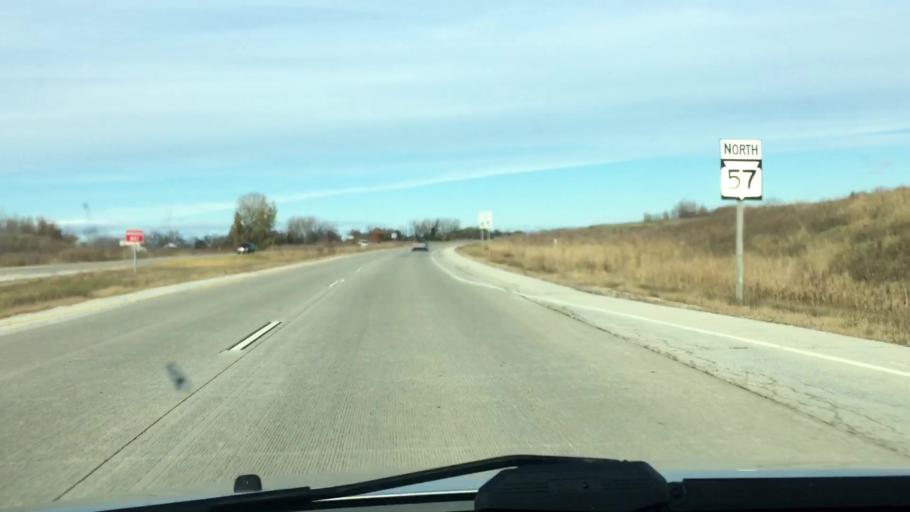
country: US
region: Wisconsin
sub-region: Kewaunee County
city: Luxemburg
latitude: 44.6476
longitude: -87.7527
